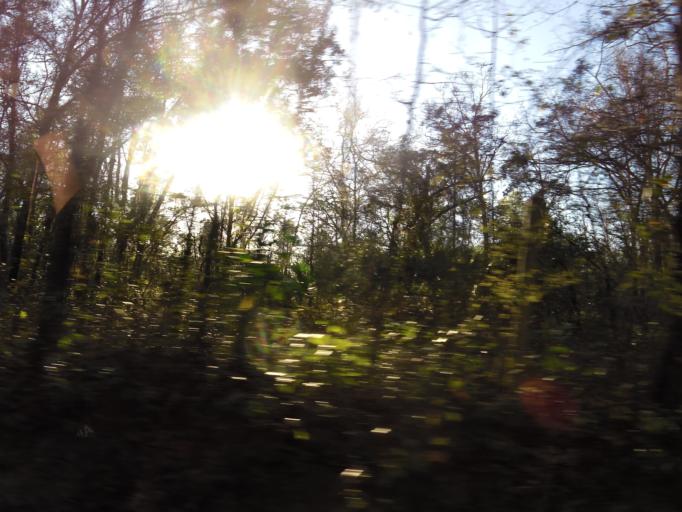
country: US
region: Florida
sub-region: Clay County
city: Middleburg
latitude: 30.1447
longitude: -81.8821
